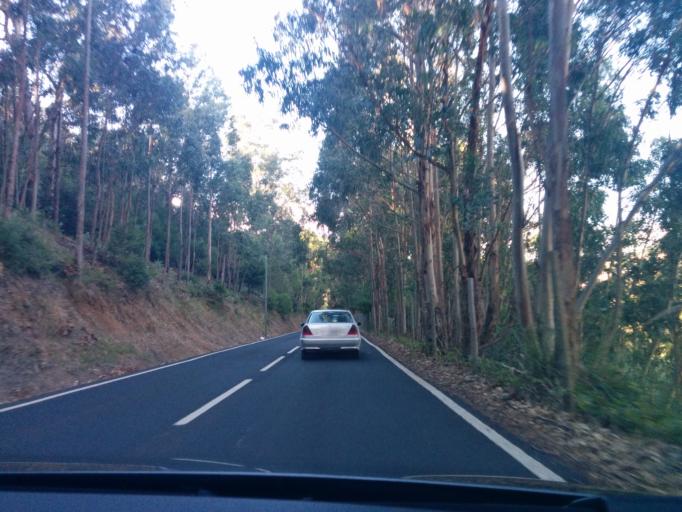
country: PT
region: Lisbon
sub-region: Cascais
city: Alcabideche
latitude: 38.7491
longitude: -9.4503
